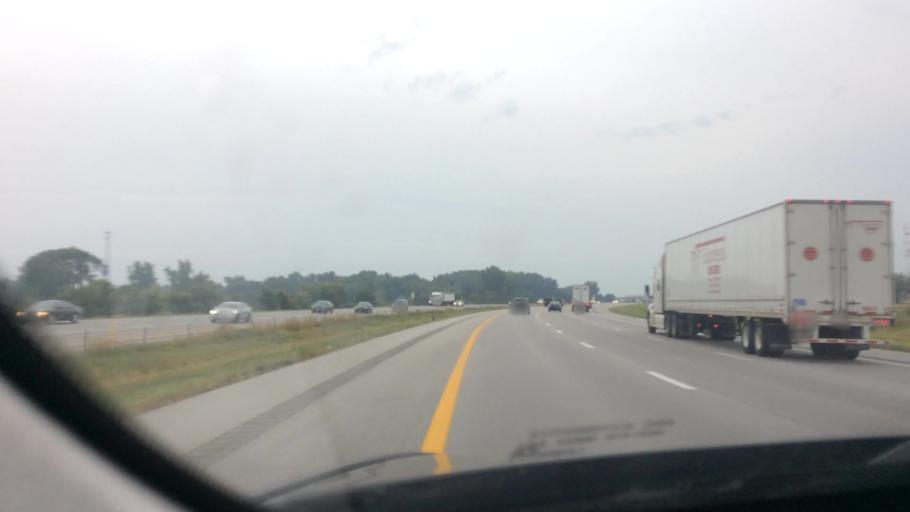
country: US
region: Ohio
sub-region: Wood County
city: North Baltimore
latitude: 41.2495
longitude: -83.6491
